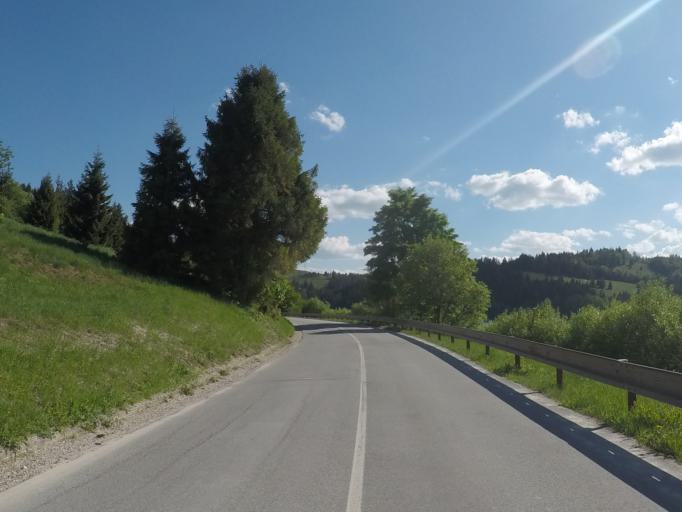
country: SK
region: Kosicky
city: Dobsina
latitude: 48.8618
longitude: 20.3855
